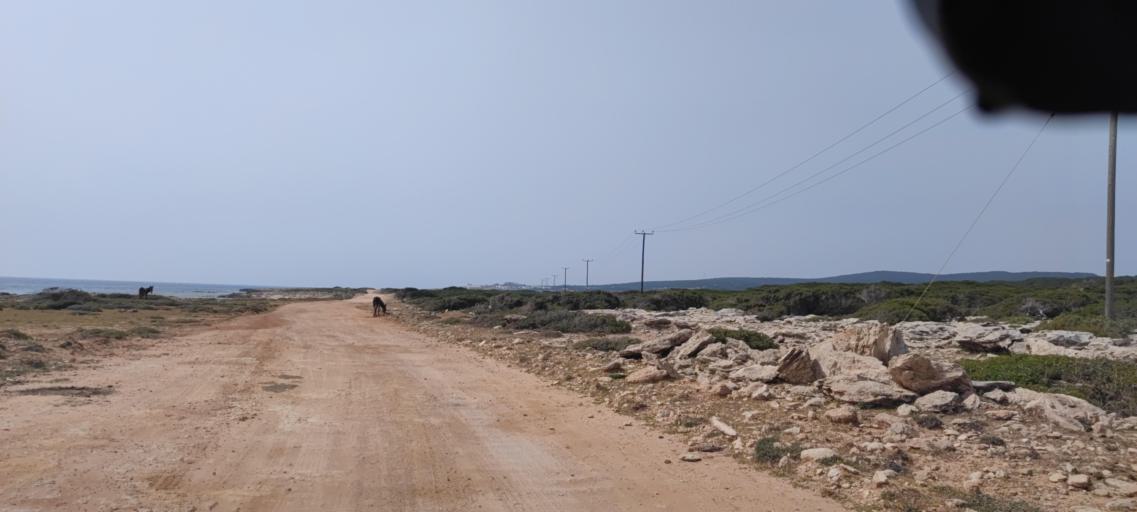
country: CY
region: Ammochostos
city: Rizokarpaso
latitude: 35.6777
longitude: 34.5778
